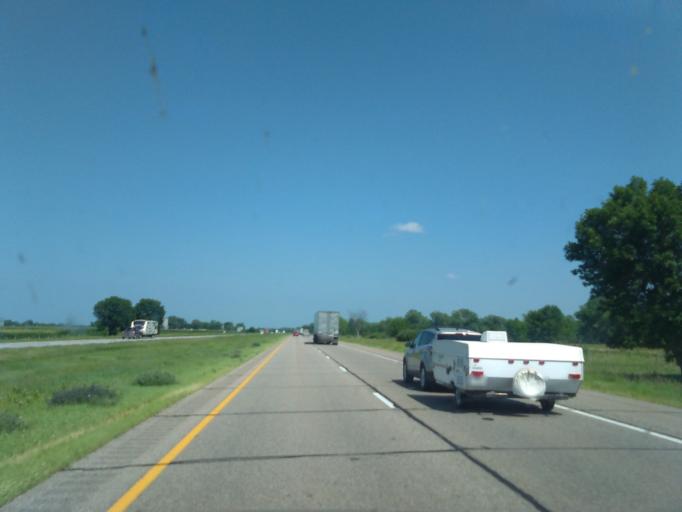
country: US
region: Nebraska
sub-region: Buffalo County
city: Kearney
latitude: 40.6742
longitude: -99.2390
